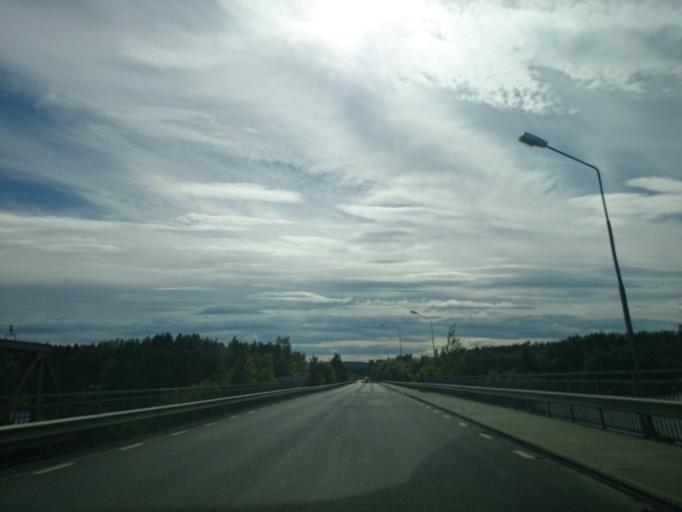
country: SE
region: Jaemtland
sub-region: Are Kommun
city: Jarpen
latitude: 63.3442
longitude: 13.4537
